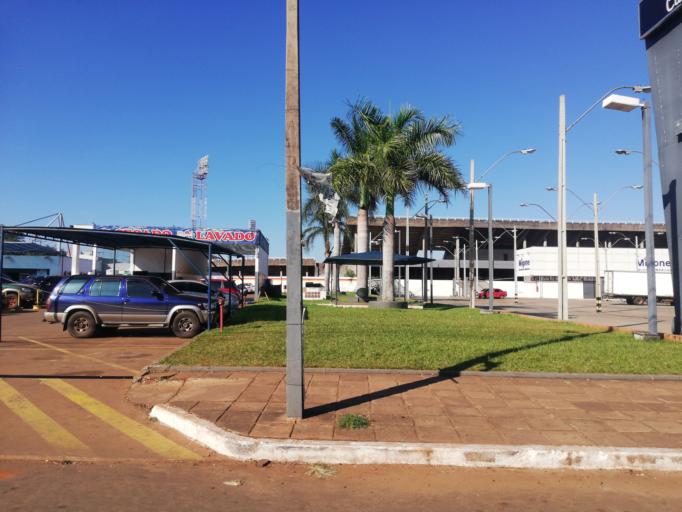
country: PY
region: Alto Parana
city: Presidente Franco
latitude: -25.5252
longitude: -54.6118
